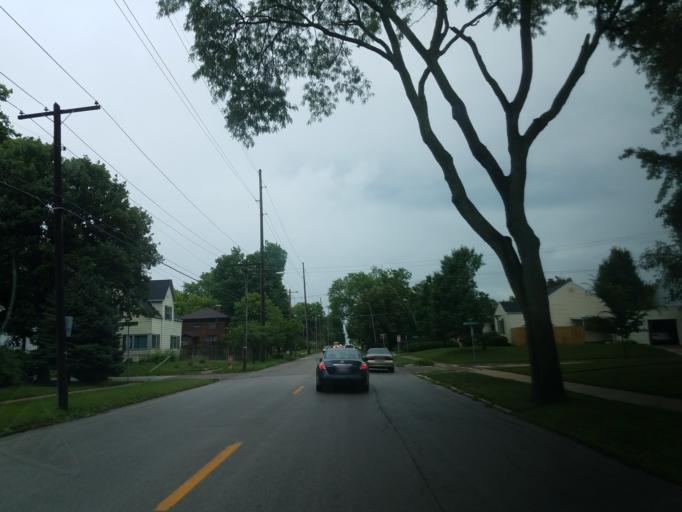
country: US
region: Illinois
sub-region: McLean County
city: Bloomington
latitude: 40.4740
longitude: -88.9733
